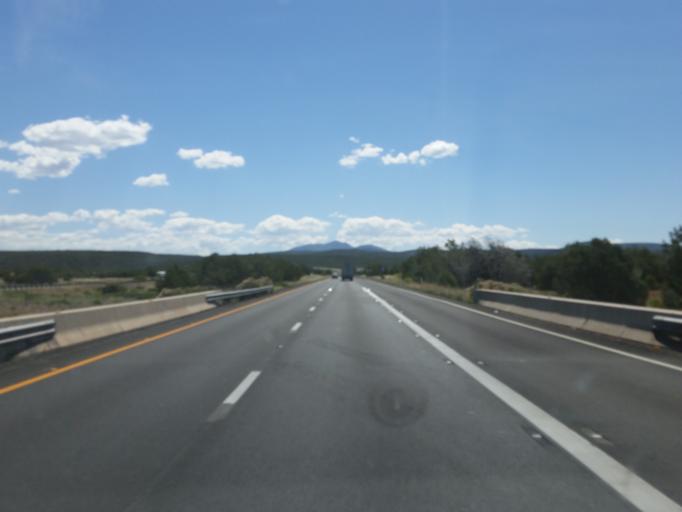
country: US
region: Arizona
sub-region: Coconino County
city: Williams
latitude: 35.2141
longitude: -112.4247
